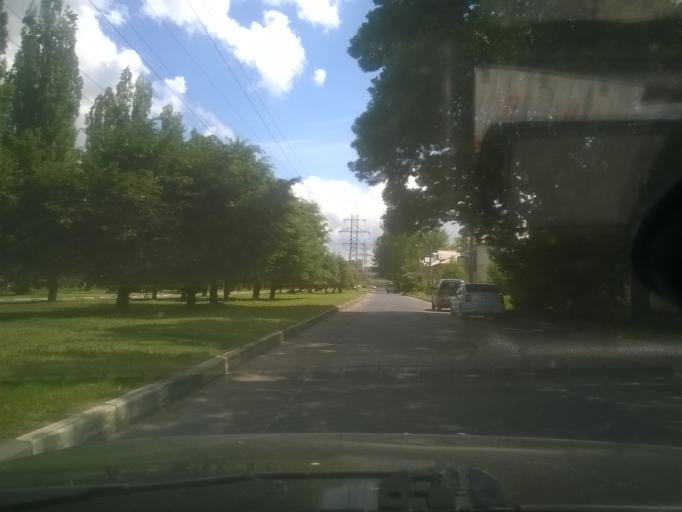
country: RU
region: Kursk
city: Kursk
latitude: 51.6658
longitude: 36.1353
